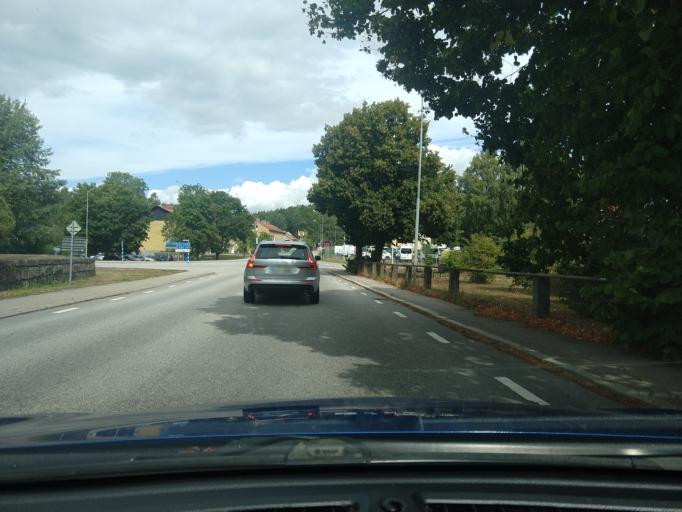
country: SE
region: Blekinge
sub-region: Ronneby Kommun
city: Brakne-Hoby
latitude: 56.3475
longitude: 15.1533
